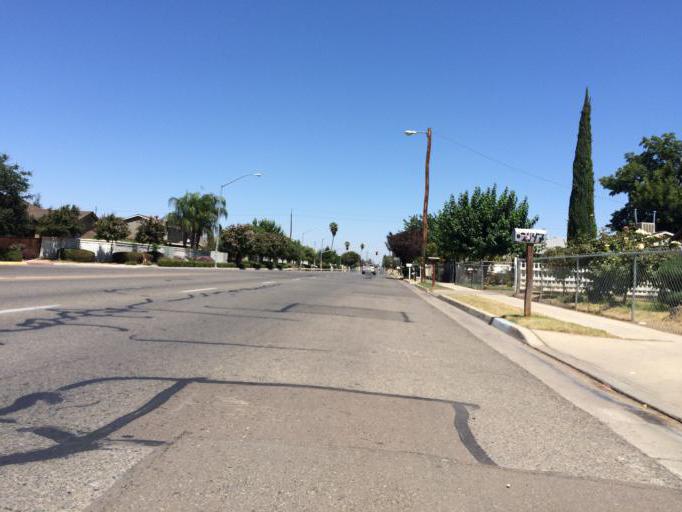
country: US
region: California
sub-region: Fresno County
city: Fresno
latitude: 36.7123
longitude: -119.7456
